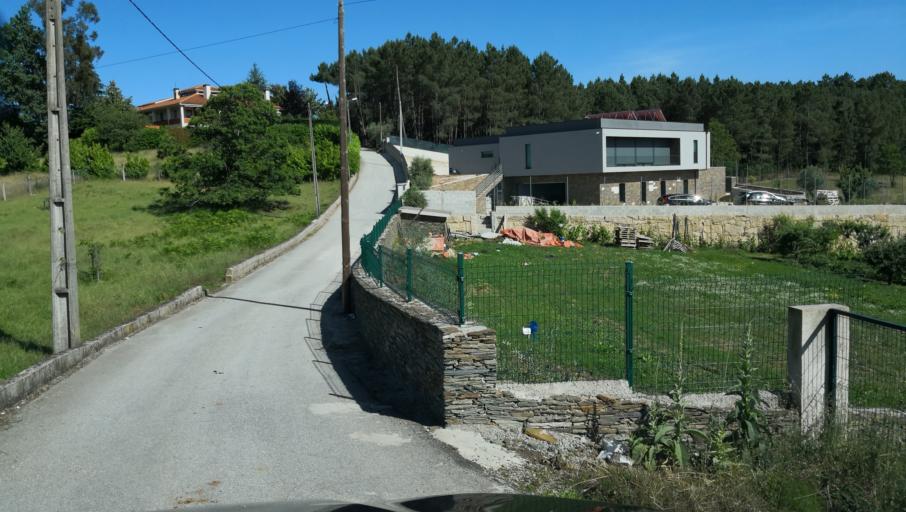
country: PT
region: Vila Real
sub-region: Vila Real
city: Vila Real
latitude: 41.2791
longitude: -7.6953
